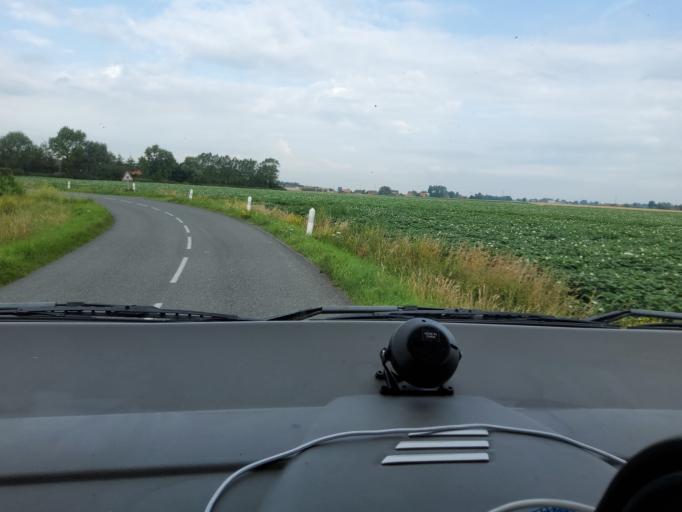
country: FR
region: Nord-Pas-de-Calais
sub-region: Departement du Nord
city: Brouckerque
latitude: 50.9543
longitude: 2.3071
